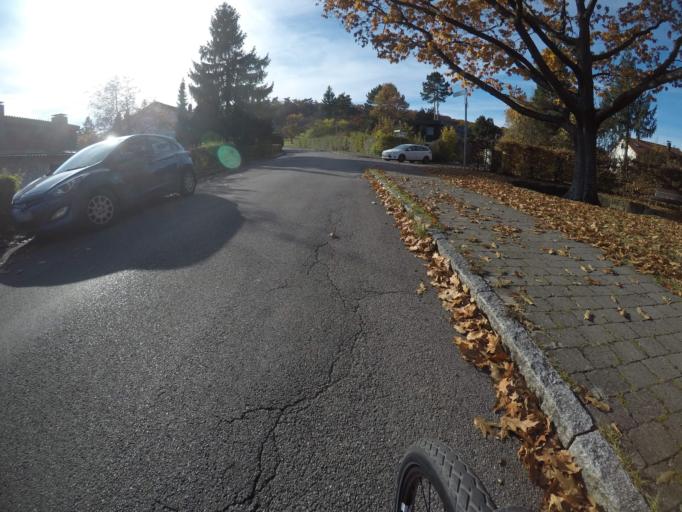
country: DE
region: Baden-Wuerttemberg
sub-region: Regierungsbezirk Stuttgart
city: Leinfelden-Echterdingen
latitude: 48.6819
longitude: 9.1534
